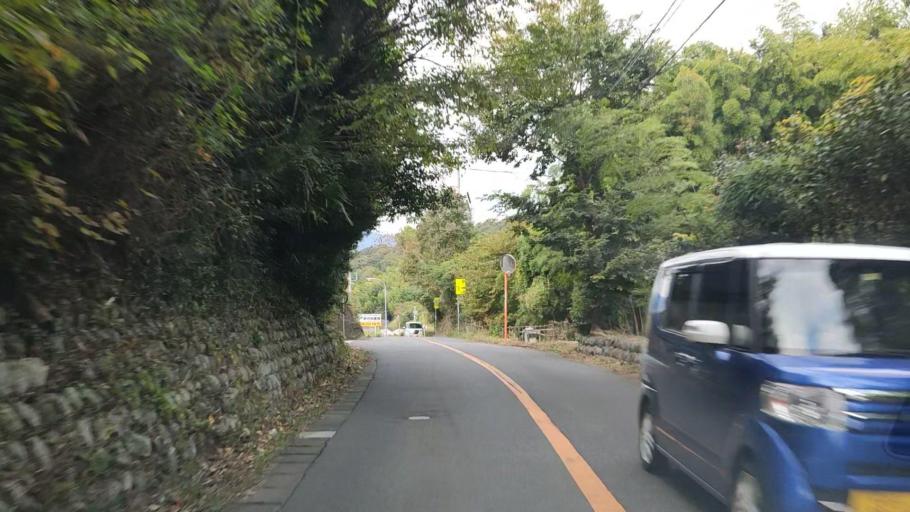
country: JP
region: Shizuoka
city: Shizuoka-shi
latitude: 34.9903
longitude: 138.4551
